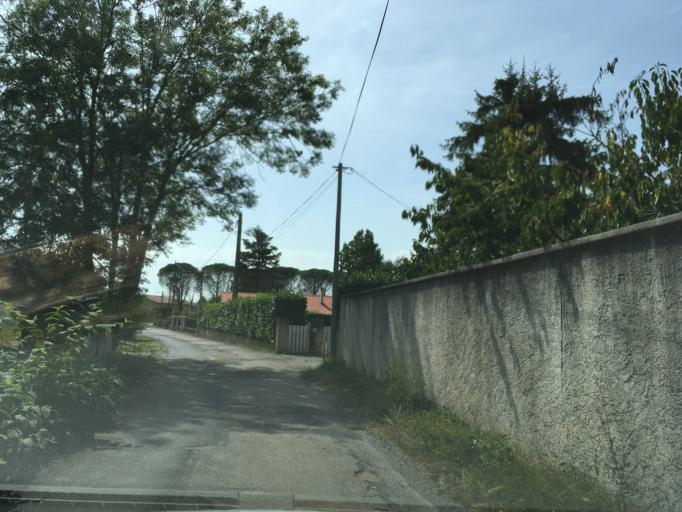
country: FR
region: Midi-Pyrenees
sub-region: Departement du Tarn
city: Castres
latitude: 43.6226
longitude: 2.2703
